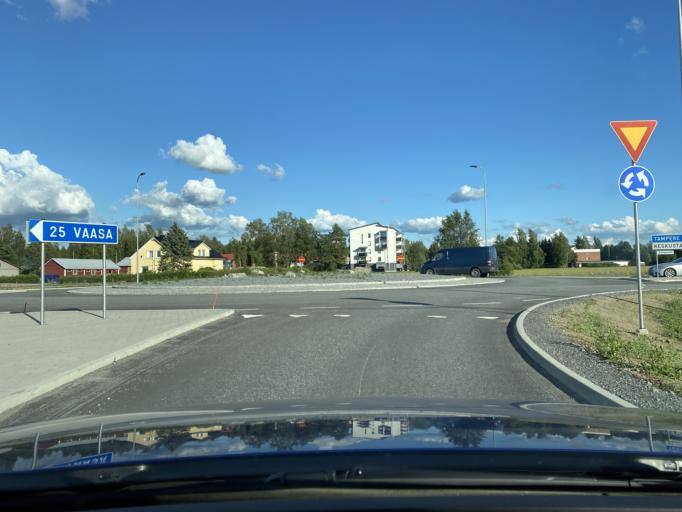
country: FI
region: Ostrobothnia
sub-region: Kyroenmaa
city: Laihia
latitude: 62.9841
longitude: 22.0063
